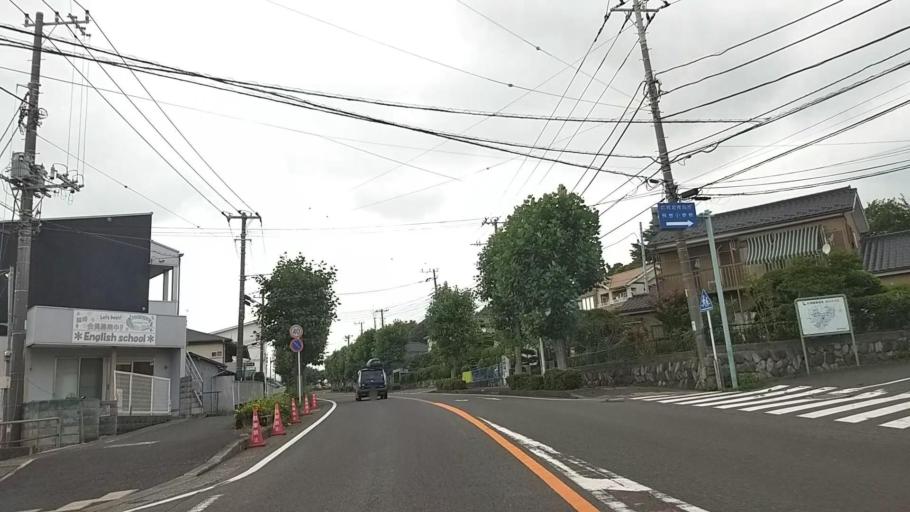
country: JP
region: Kanagawa
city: Isehara
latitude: 35.3880
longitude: 139.3158
